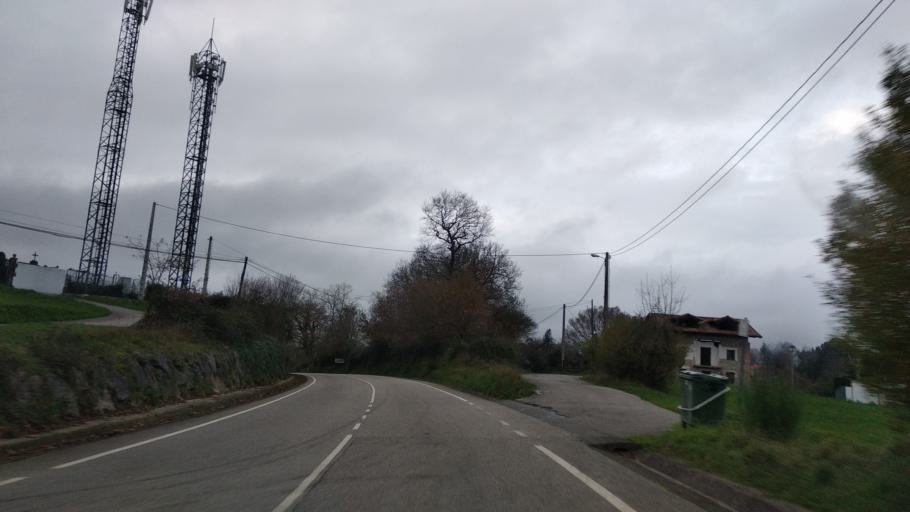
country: ES
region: Cantabria
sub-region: Provincia de Cantabria
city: Entrambasaguas
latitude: 43.4170
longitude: -3.7027
